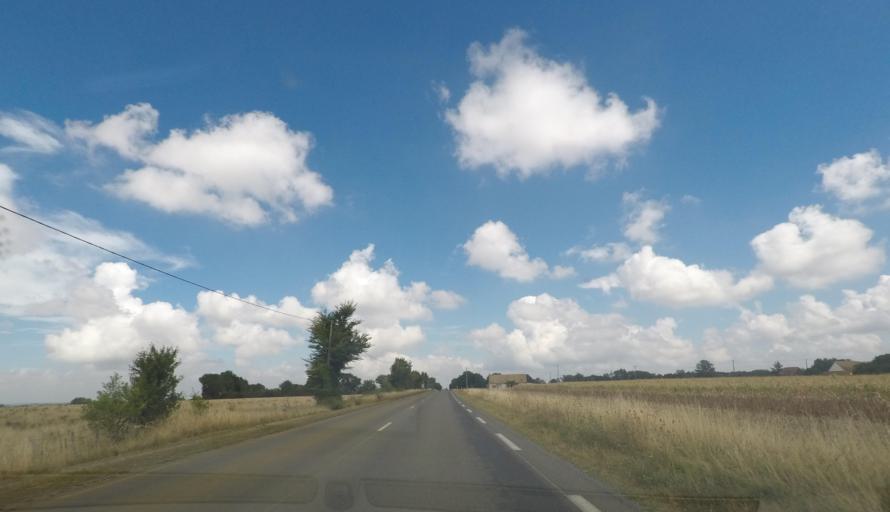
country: FR
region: Pays de la Loire
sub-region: Departement de la Sarthe
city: Saint-Cosme-en-Vairais
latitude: 48.2330
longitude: 0.4340
